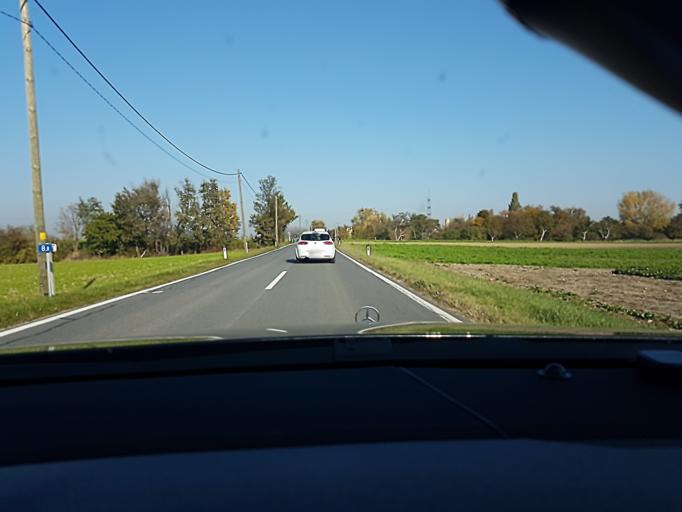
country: AT
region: Lower Austria
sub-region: Politischer Bezirk Modling
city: Achau
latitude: 48.0848
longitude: 16.4013
